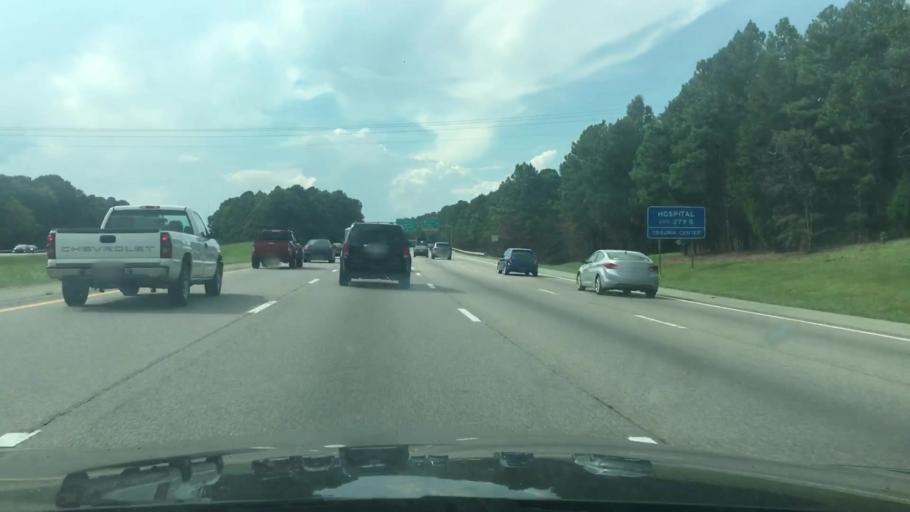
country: US
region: North Carolina
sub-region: Wake County
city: Morrisville
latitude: 35.8966
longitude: -78.8638
